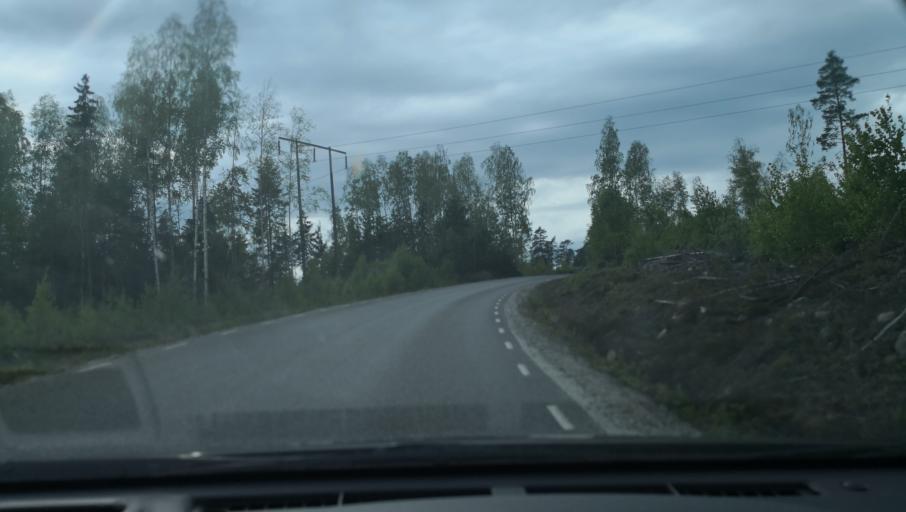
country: SE
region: Vaestmanland
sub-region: Skinnskattebergs Kommun
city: Skinnskatteberg
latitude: 59.8233
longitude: 15.5843
